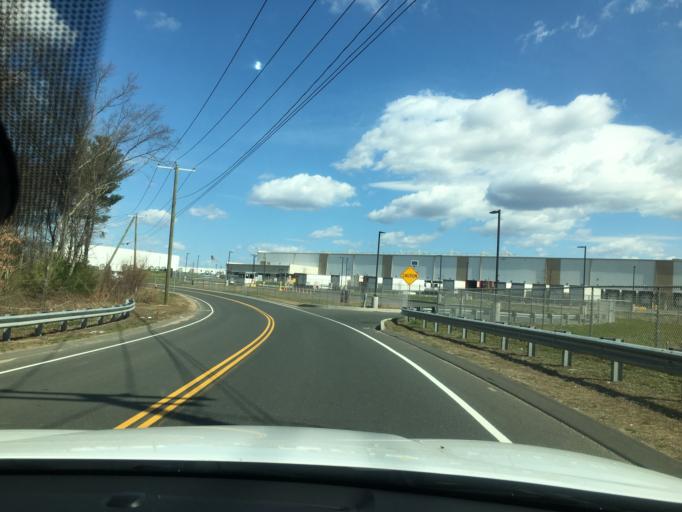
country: US
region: Connecticut
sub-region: Hartford County
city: Blue Hills
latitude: 41.8659
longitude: -72.7088
